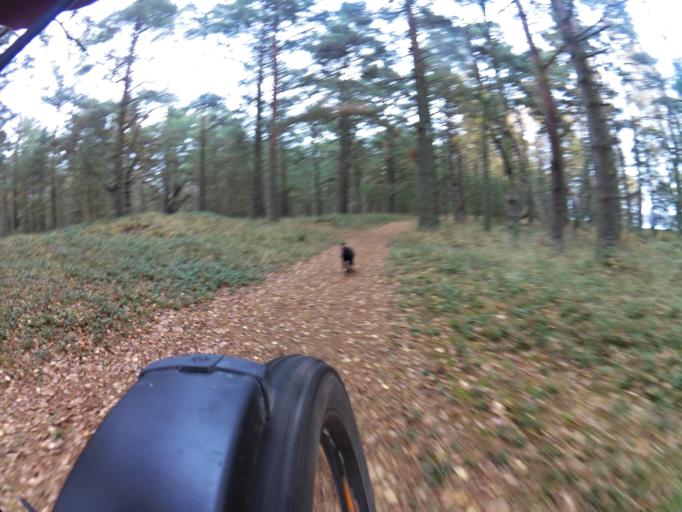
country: PL
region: Pomeranian Voivodeship
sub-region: Powiat leborski
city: Leba
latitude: 54.7677
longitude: 17.6156
